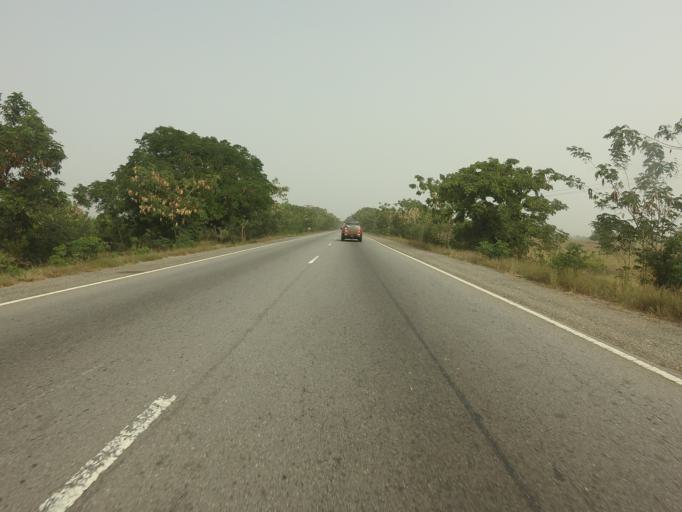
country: GH
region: Volta
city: Anloga
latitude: 5.8881
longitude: 0.4595
